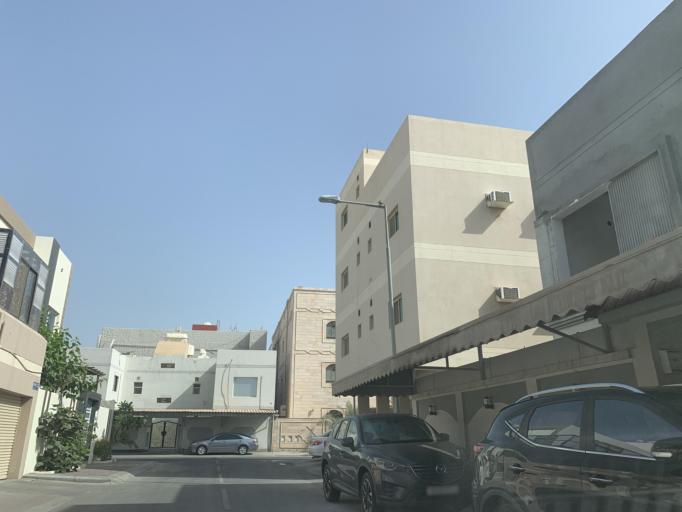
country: BH
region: Northern
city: Ar Rifa'
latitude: 26.1480
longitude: 50.5823
